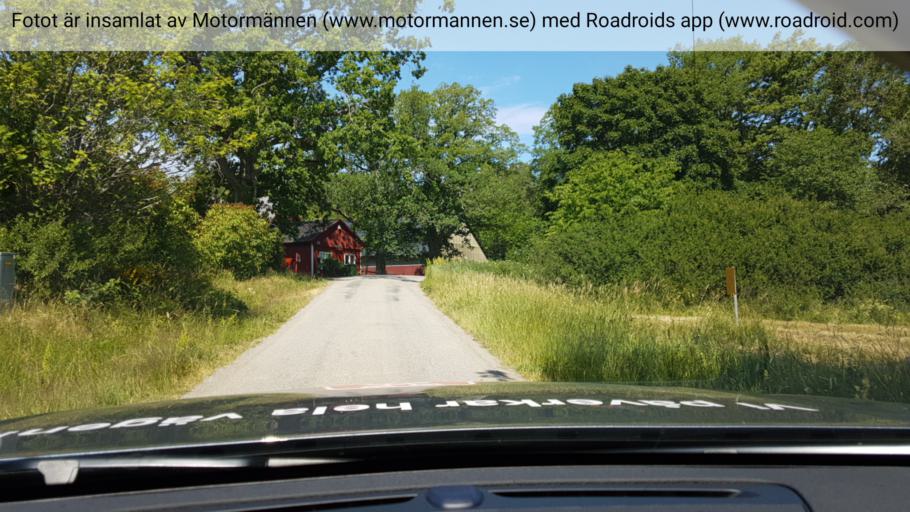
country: SE
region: Stockholm
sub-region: Haninge Kommun
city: Jordbro
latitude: 59.0142
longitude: 18.1148
